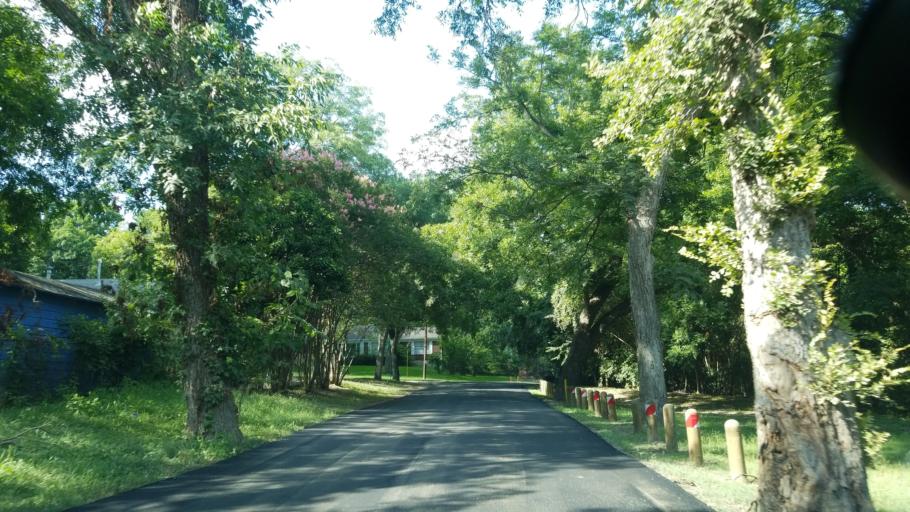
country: US
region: Texas
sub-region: Dallas County
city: Dallas
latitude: 32.7683
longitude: -96.7130
